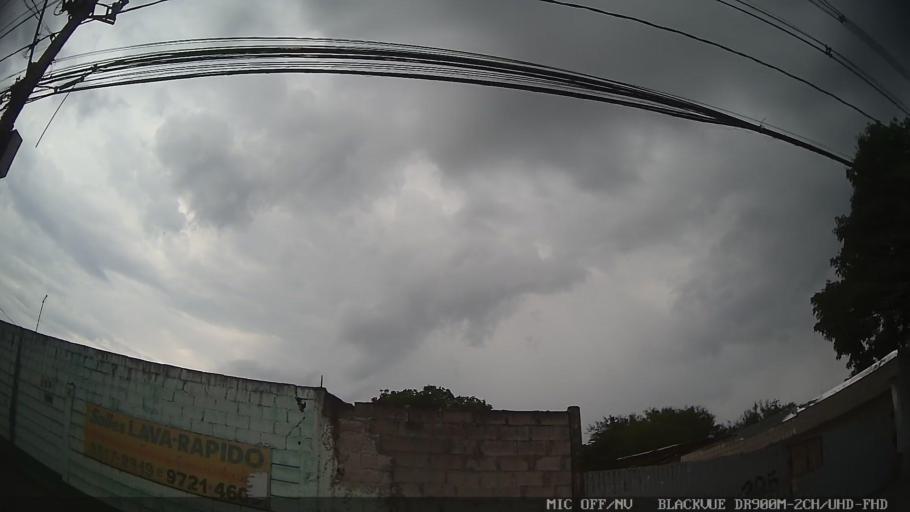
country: BR
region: Sao Paulo
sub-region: Amparo
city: Amparo
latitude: -22.7108
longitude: -46.8146
